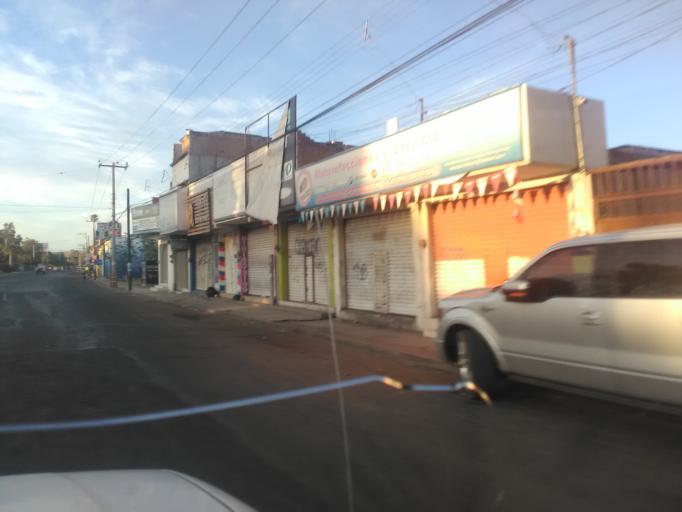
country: MX
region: Durango
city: Victoria de Durango
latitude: 24.0006
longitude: -104.6624
